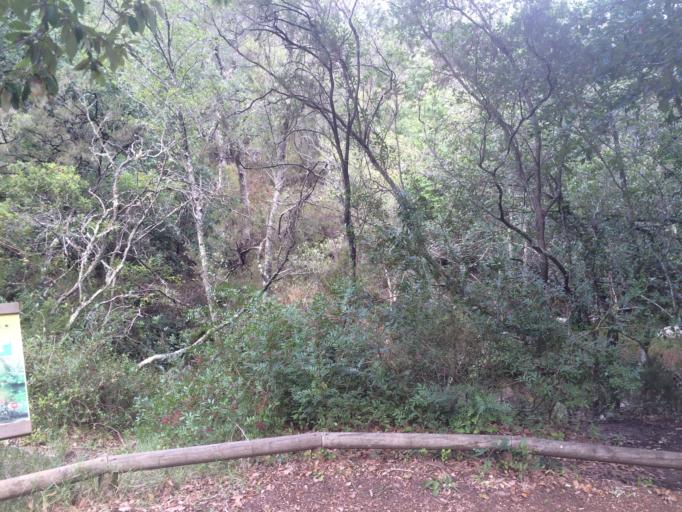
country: ES
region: Andalusia
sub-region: Provincia de Cadiz
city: Los Barrios
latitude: 36.2289
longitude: -5.6033
